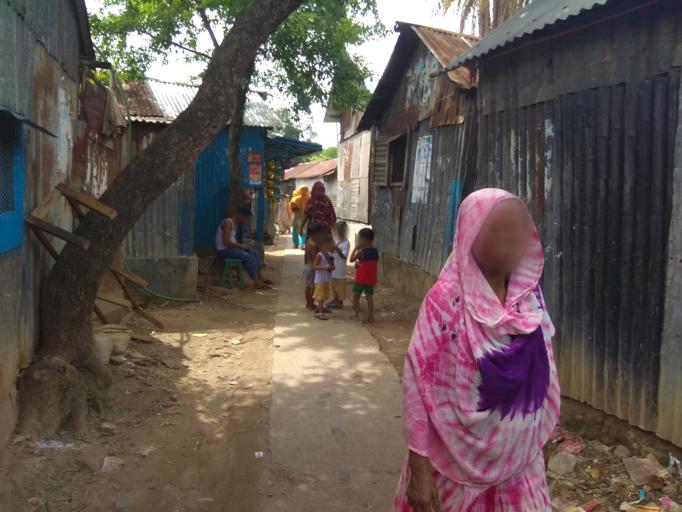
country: BD
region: Dhaka
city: Paltan
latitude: 23.8115
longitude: 90.3898
